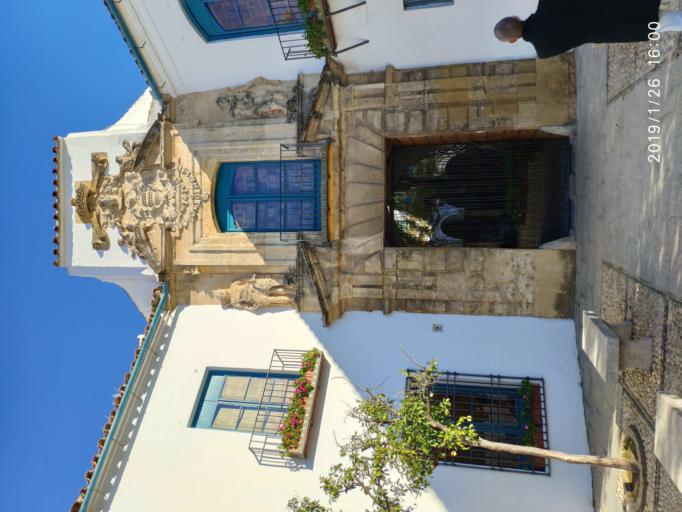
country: ES
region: Andalusia
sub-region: Province of Cordoba
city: Cordoba
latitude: 37.8886
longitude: -4.7742
